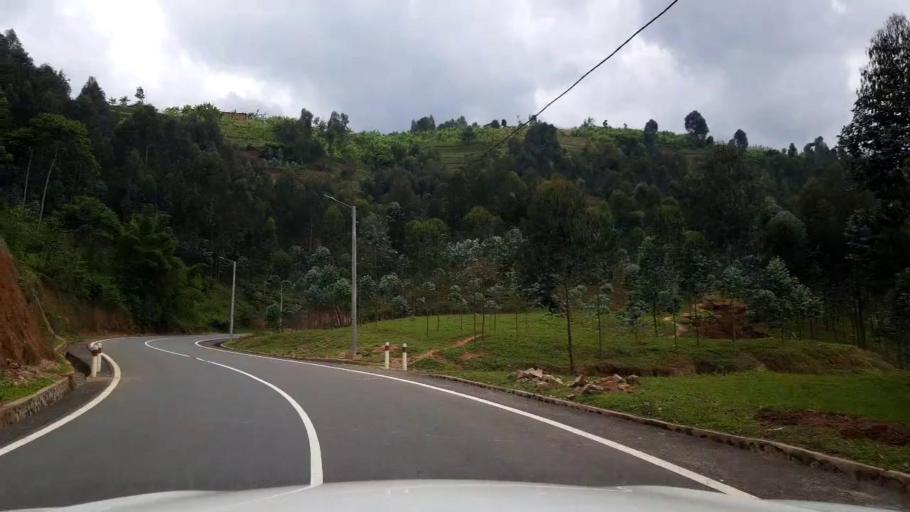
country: RW
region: Western Province
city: Kibuye
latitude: -1.9258
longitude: 29.3725
